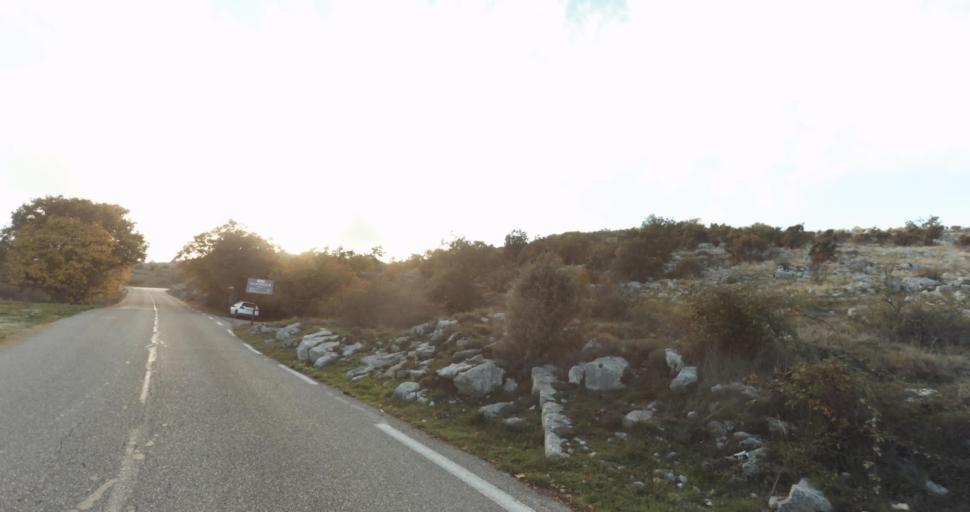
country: FR
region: Provence-Alpes-Cote d'Azur
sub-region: Departement des Alpes-Maritimes
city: Vence
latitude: 43.7633
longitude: 7.0850
